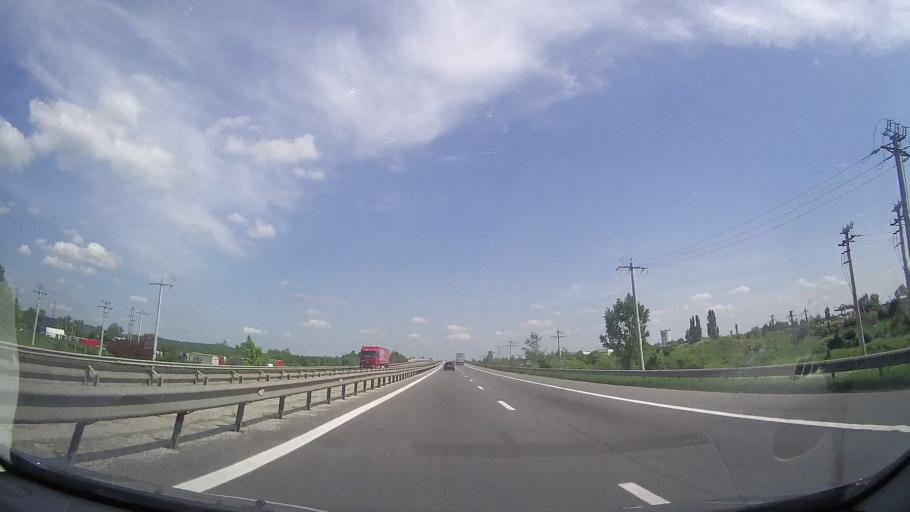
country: RO
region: Arges
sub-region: Comuna Bascov
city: Bascov
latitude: 44.8902
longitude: 24.8479
